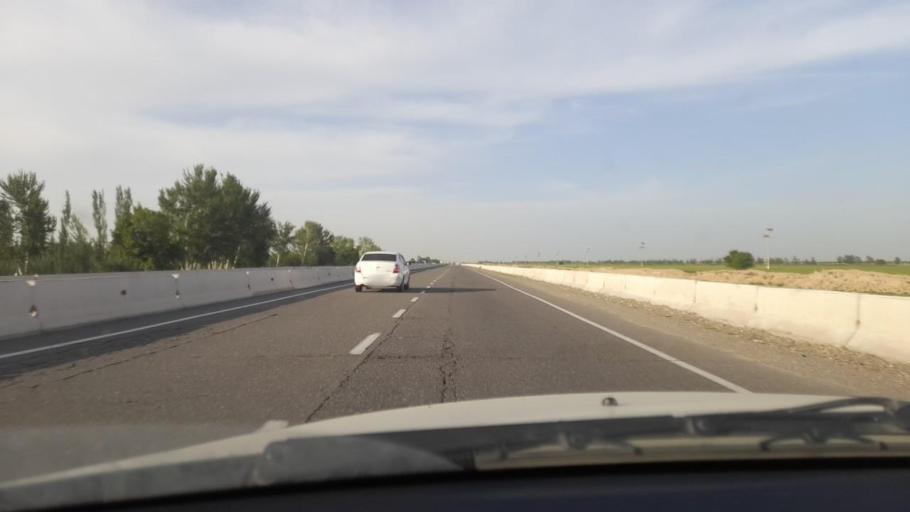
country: UZ
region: Jizzax
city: Paxtakor
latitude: 40.3385
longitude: 68.1167
